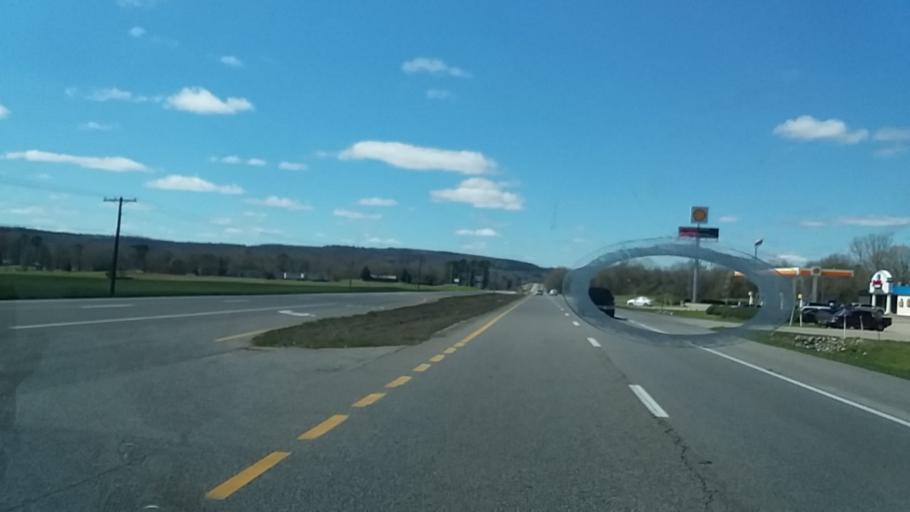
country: US
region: Alabama
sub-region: Colbert County
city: Tuscumbia
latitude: 34.7095
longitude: -87.7434
